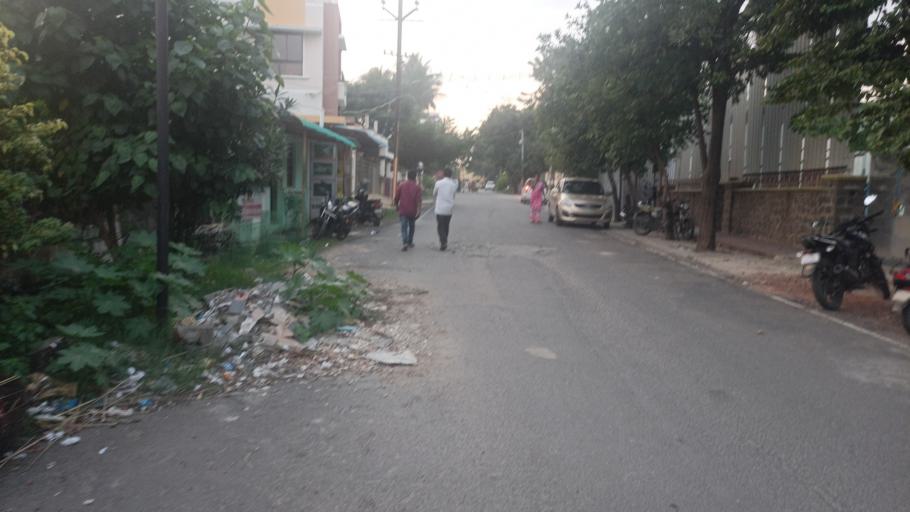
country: IN
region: Tamil Nadu
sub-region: Salem
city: Salem
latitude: 11.6738
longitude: 78.1219
